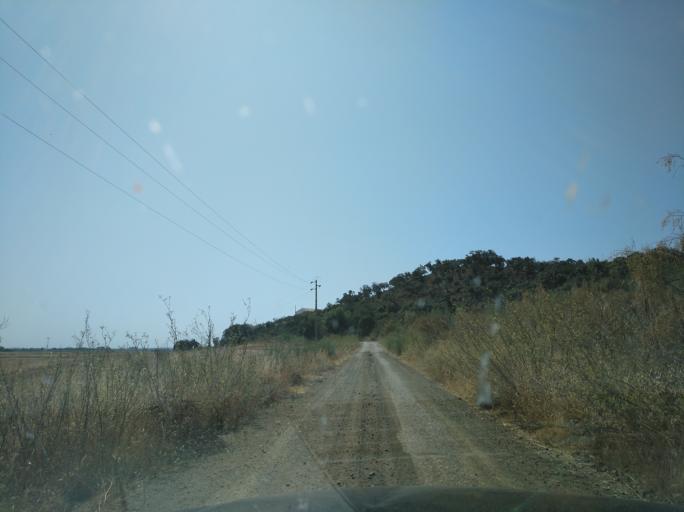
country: PT
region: Portalegre
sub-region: Campo Maior
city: Campo Maior
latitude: 39.0539
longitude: -7.0023
